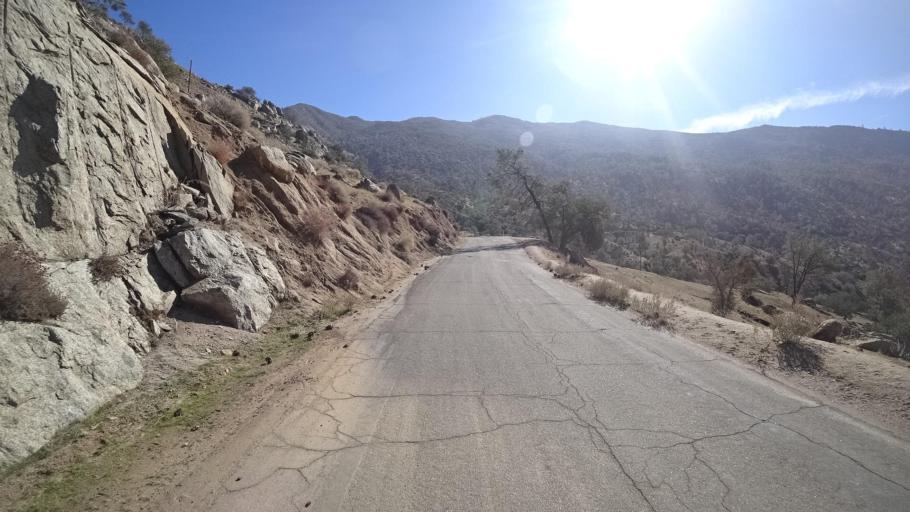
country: US
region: California
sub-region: Kern County
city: Bodfish
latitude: 35.5598
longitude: -118.5799
